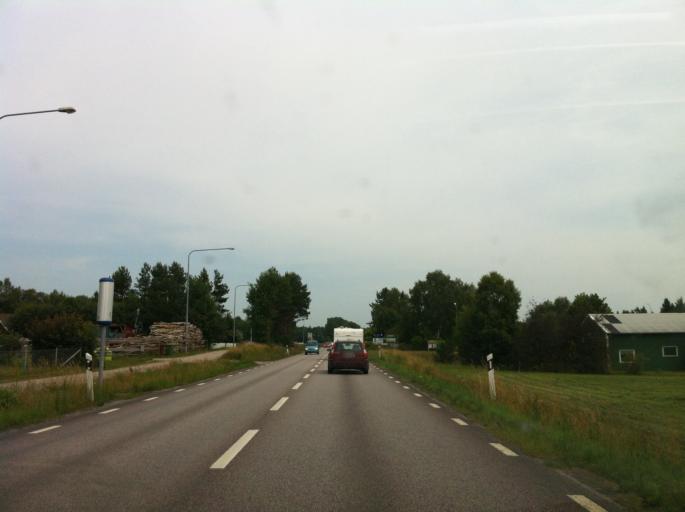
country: SE
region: Blekinge
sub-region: Karlskrona Kommun
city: Jaemjoe
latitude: 56.1959
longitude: 15.8481
